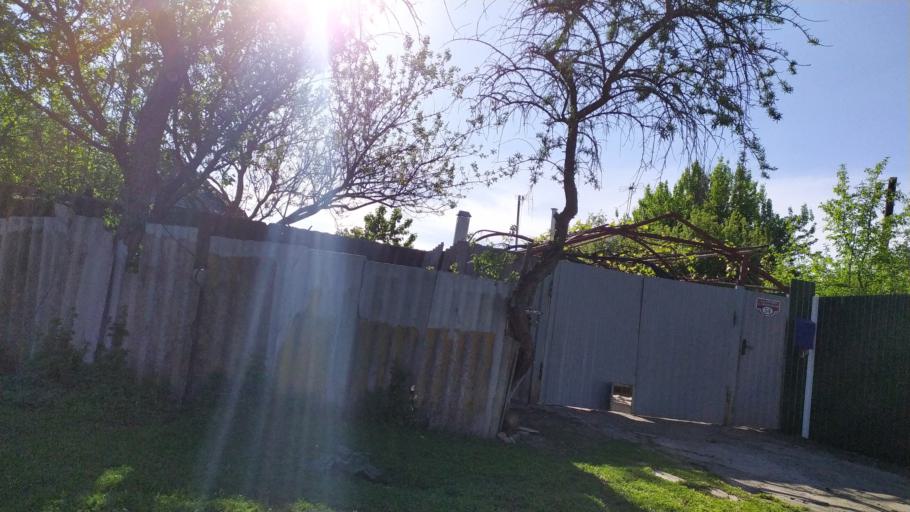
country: RU
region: Kursk
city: Kursk
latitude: 51.6329
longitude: 36.1488
